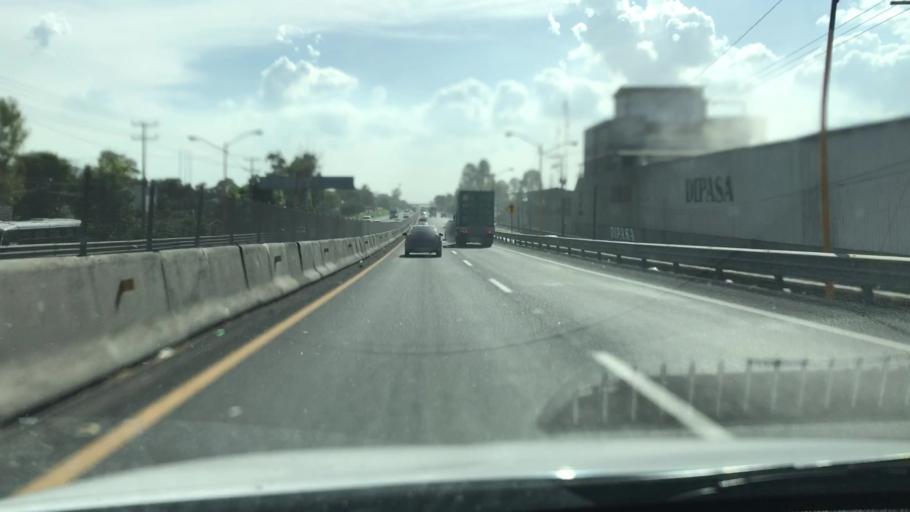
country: MX
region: Guanajuato
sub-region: Cortazar
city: Colonia la Calzada (La Olla)
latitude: 20.5109
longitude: -100.9579
